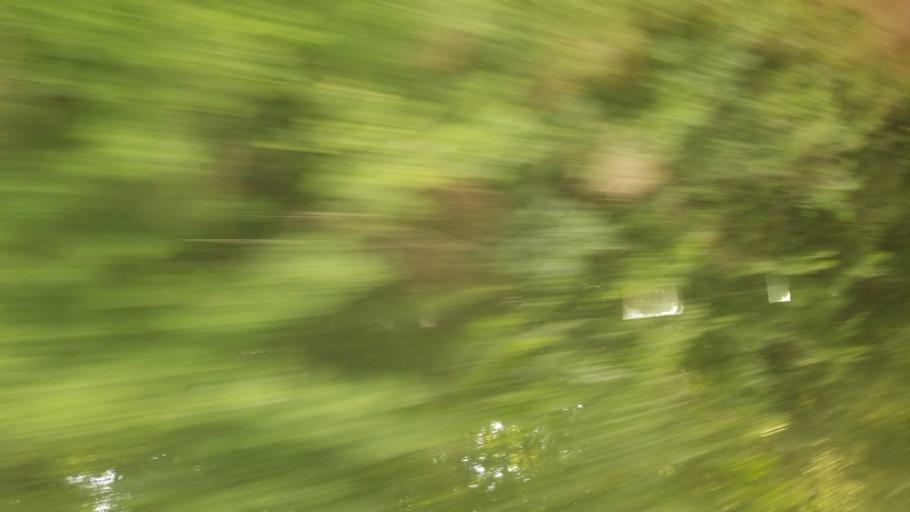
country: US
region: Kansas
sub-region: Douglas County
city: Eudora
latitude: 38.9564
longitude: -95.0787
